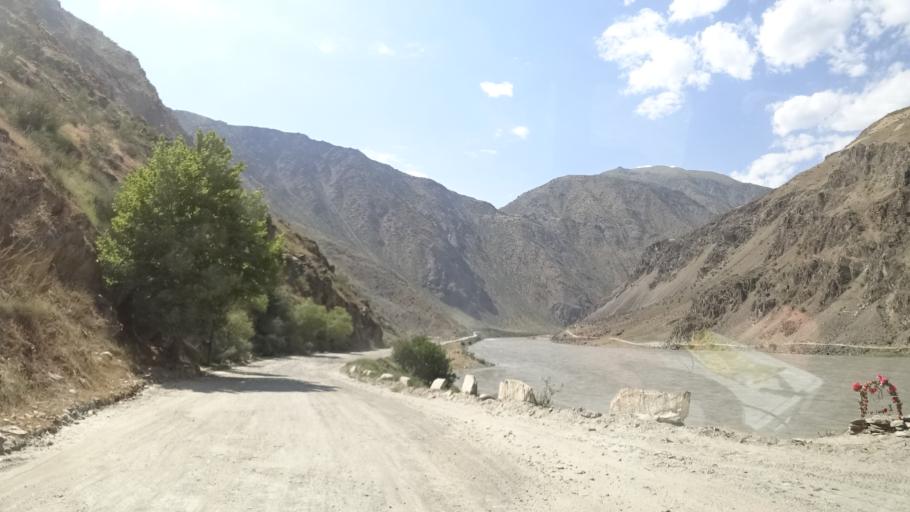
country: AF
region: Badakhshan
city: Maymay
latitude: 38.4598
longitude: 70.9579
